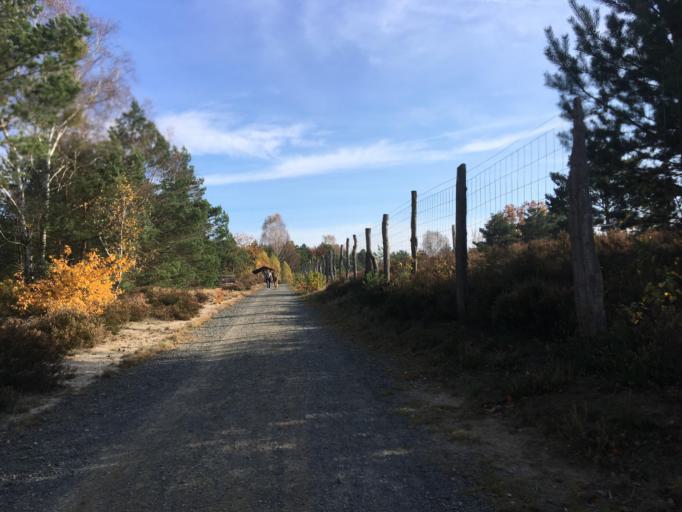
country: DE
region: Berlin
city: Buch
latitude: 52.6942
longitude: 13.5064
